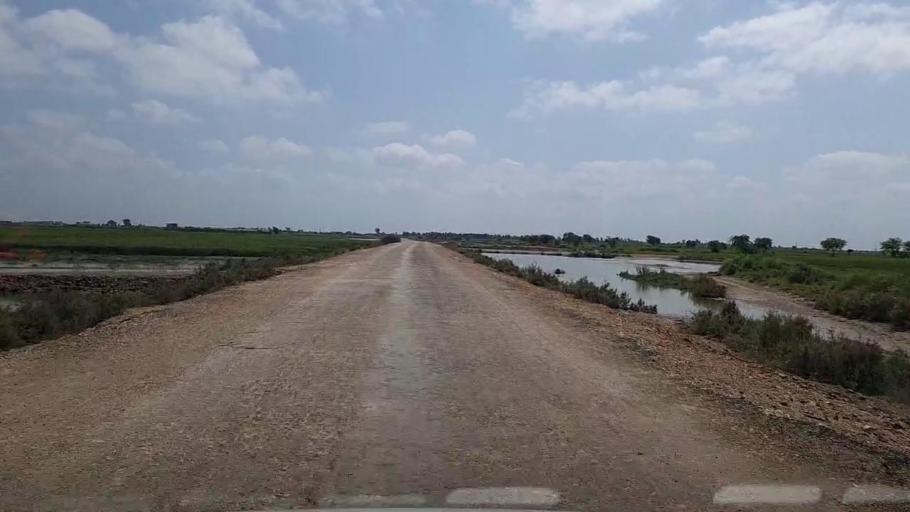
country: PK
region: Sindh
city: Talhar
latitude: 24.8841
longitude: 68.7070
